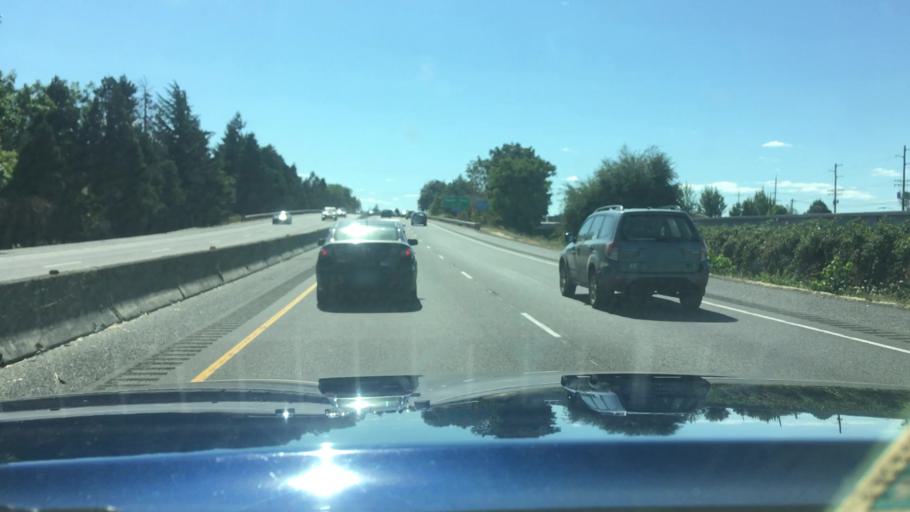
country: US
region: Oregon
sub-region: Lane County
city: Springfield
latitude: 44.0618
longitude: -123.0160
